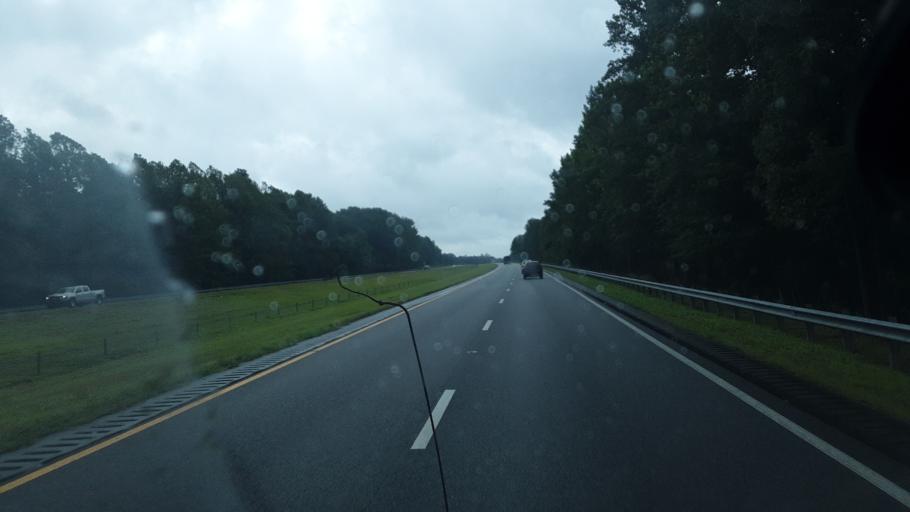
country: US
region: North Carolina
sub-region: Davidson County
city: Wallburg
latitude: 36.0304
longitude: -80.0715
